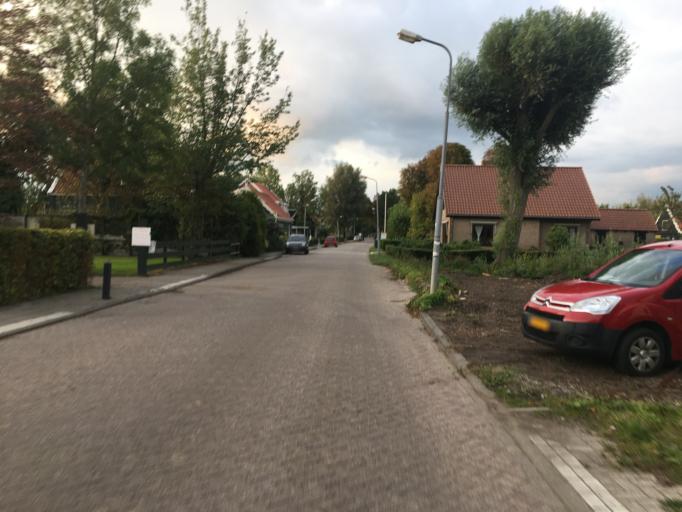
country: NL
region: North Holland
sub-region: Gemeente Zaanstad
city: Zaanstad
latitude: 52.4412
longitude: 4.7781
